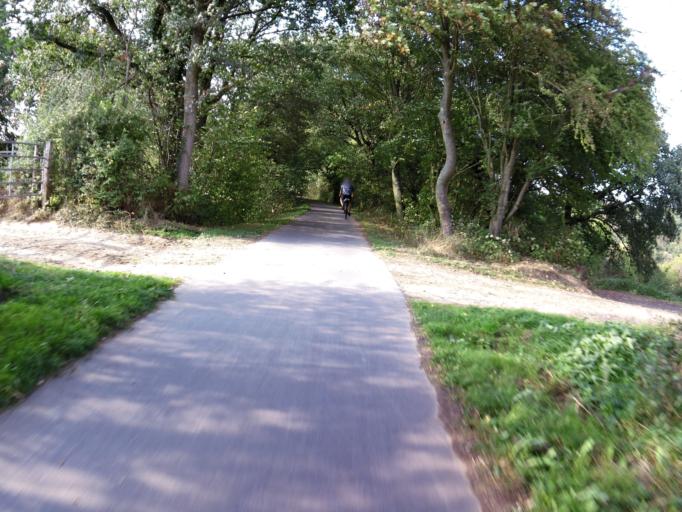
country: DE
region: North Rhine-Westphalia
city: Stolberg
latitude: 50.7195
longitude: 6.1953
